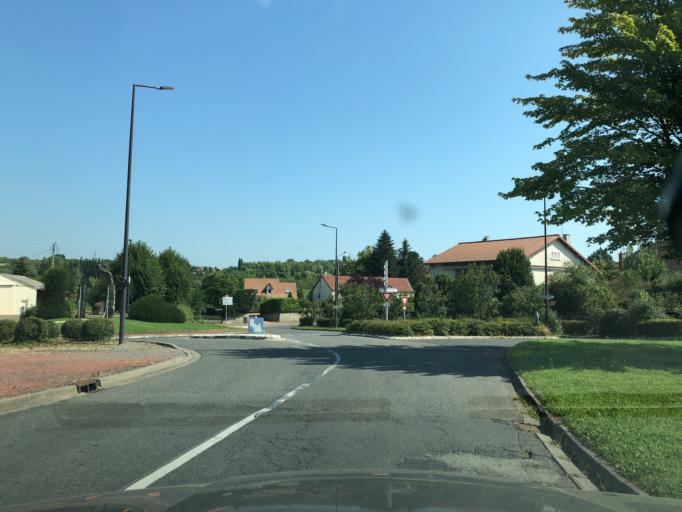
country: FR
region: Auvergne
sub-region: Departement de l'Allier
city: Cusset
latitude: 46.1355
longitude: 3.4665
